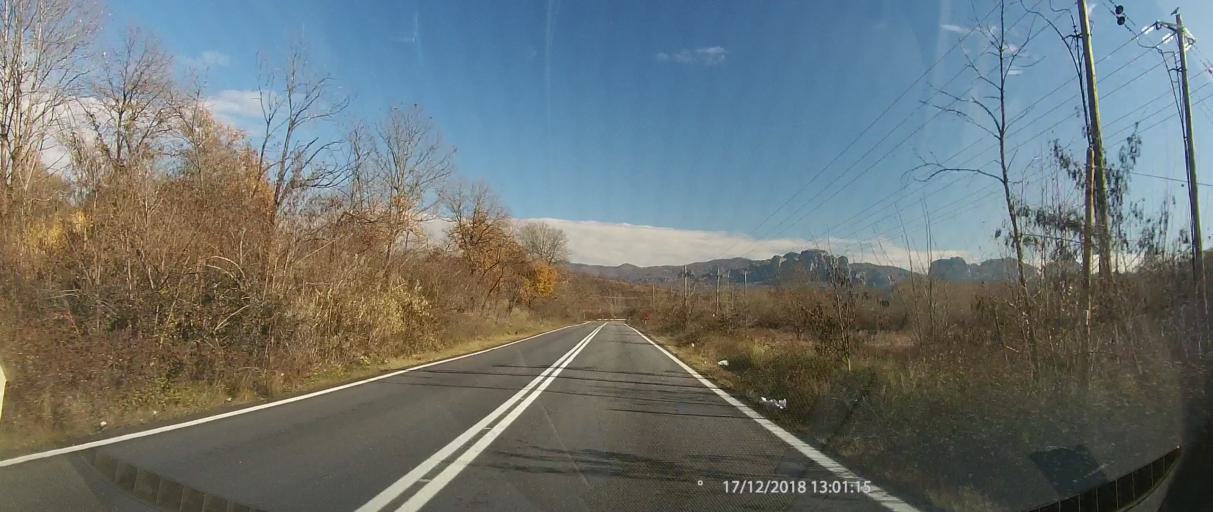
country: GR
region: Thessaly
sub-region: Trikala
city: Kastraki
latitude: 39.7324
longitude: 21.5792
